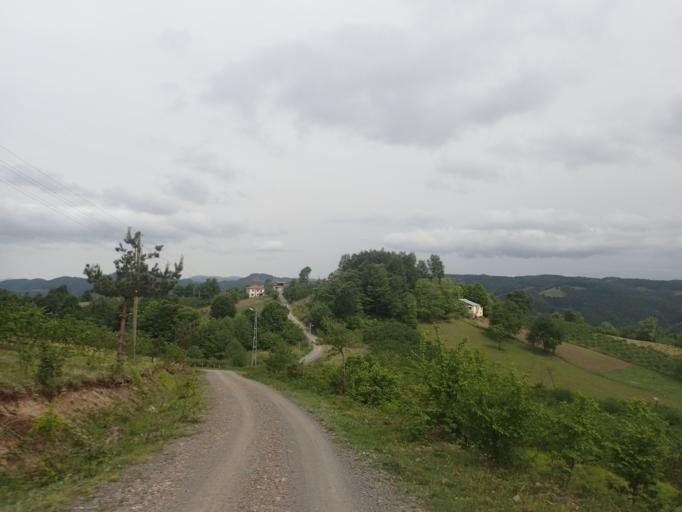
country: TR
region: Ordu
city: Akkus
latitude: 40.8898
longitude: 37.0732
